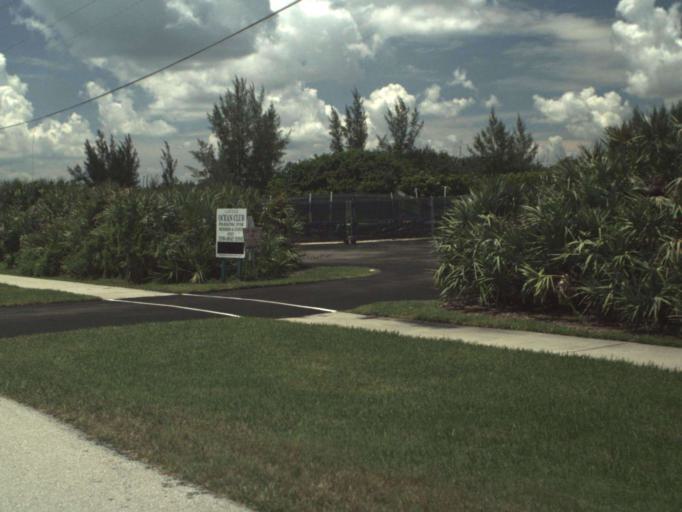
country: US
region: Florida
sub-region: Martin County
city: Sewall's Point
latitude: 27.2232
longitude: -80.1803
